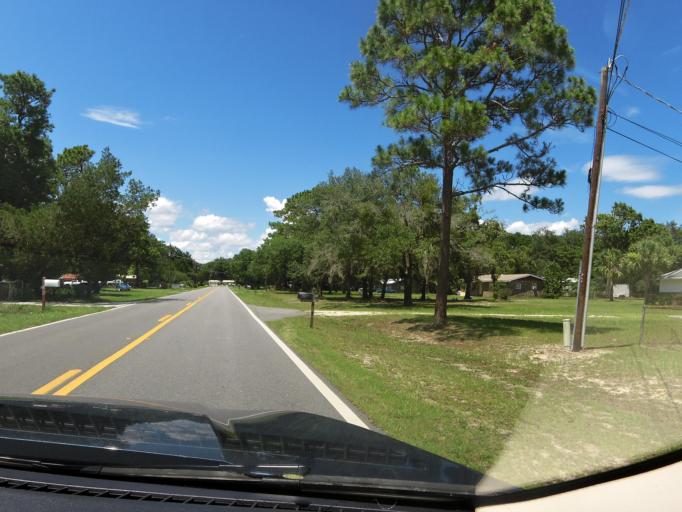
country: US
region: Georgia
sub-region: Camden County
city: St. Marys
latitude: 30.6765
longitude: -81.5397
